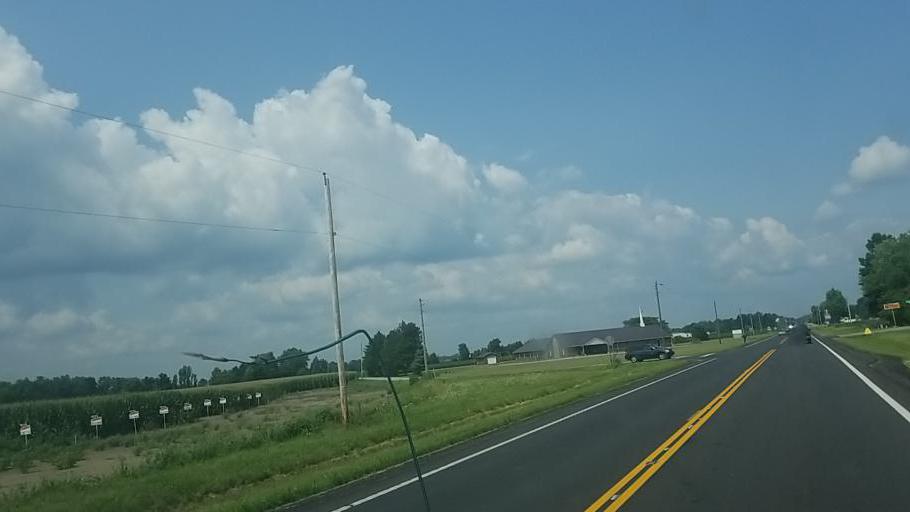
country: US
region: Ohio
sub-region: Crawford County
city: Bucyrus
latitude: 40.7773
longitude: -82.9982
